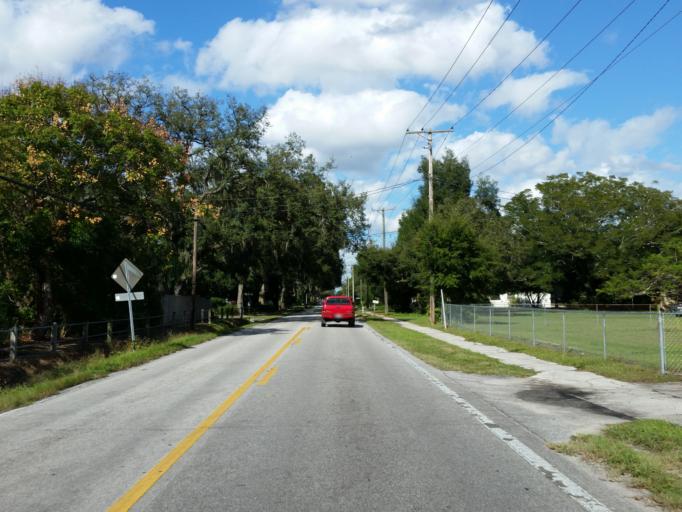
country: US
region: Florida
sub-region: Hillsborough County
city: Brandon
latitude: 27.9091
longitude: -82.2775
